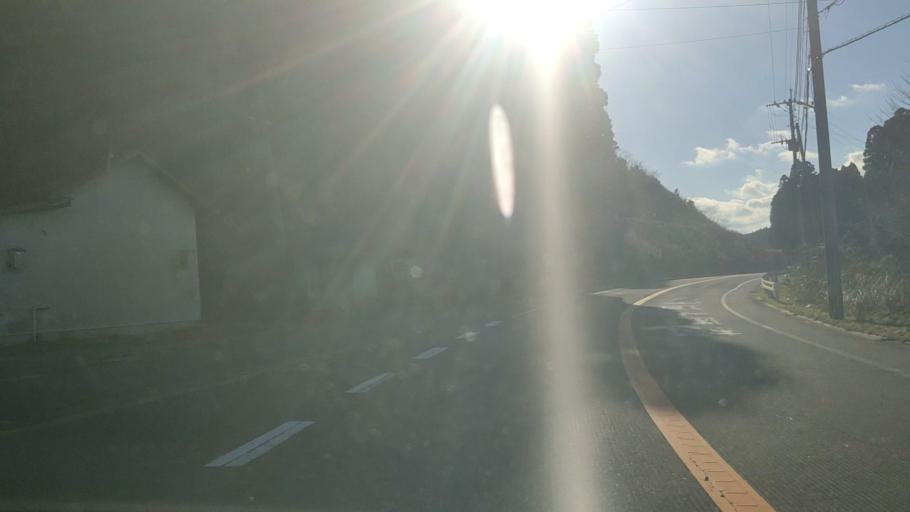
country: JP
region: Fukuoka
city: Maebaru-chuo
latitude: 33.4418
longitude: 130.2686
